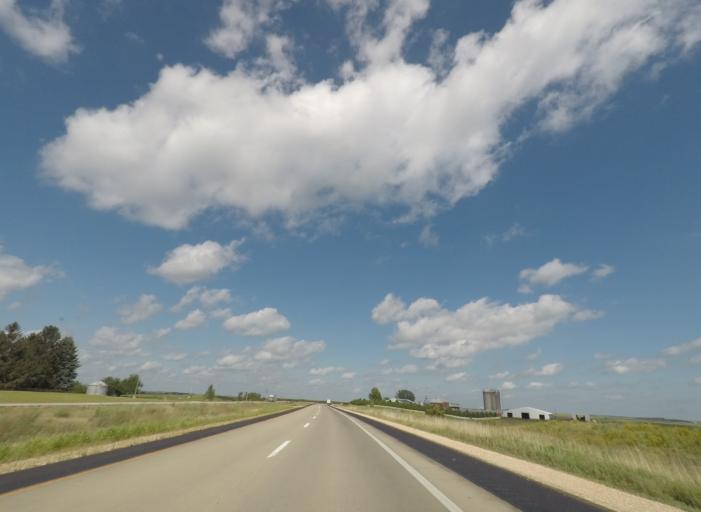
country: US
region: Iowa
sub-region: Dubuque County
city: Cascade
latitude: 42.2884
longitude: -91.0735
